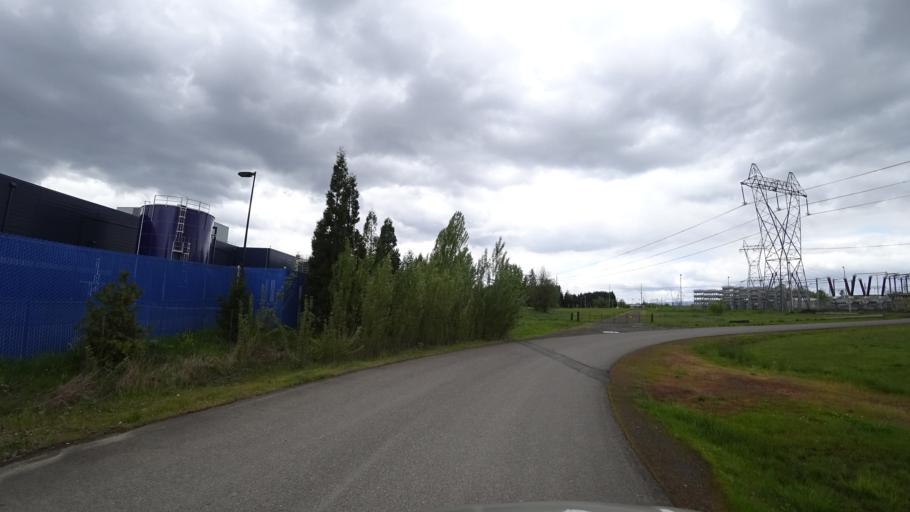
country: US
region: Oregon
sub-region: Washington County
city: Rockcreek
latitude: 45.5480
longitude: -122.8962
